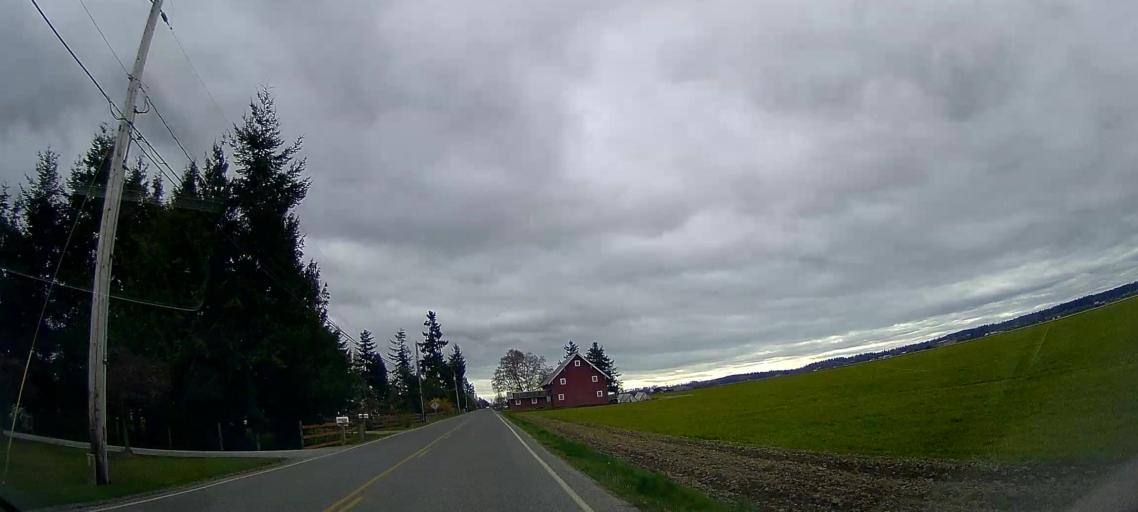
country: US
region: Washington
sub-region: Skagit County
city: Mount Vernon
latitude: 48.4058
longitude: -122.4010
